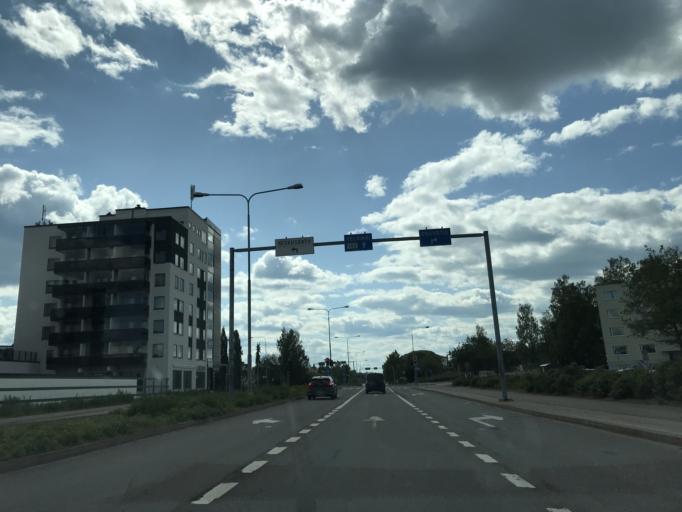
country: FI
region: Uusimaa
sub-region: Helsinki
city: Maentsaelae
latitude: 60.6362
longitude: 25.3170
